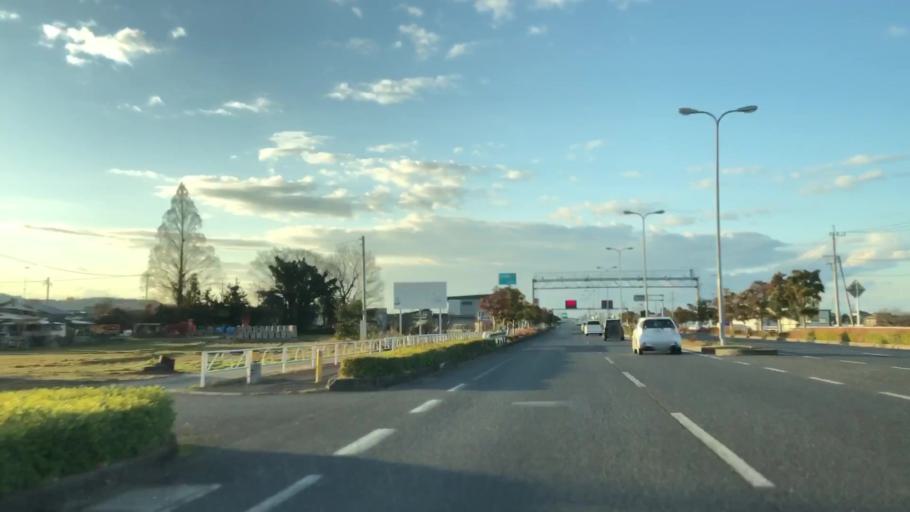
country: JP
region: Fukuoka
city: Nakatsu
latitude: 33.5448
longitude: 131.2853
